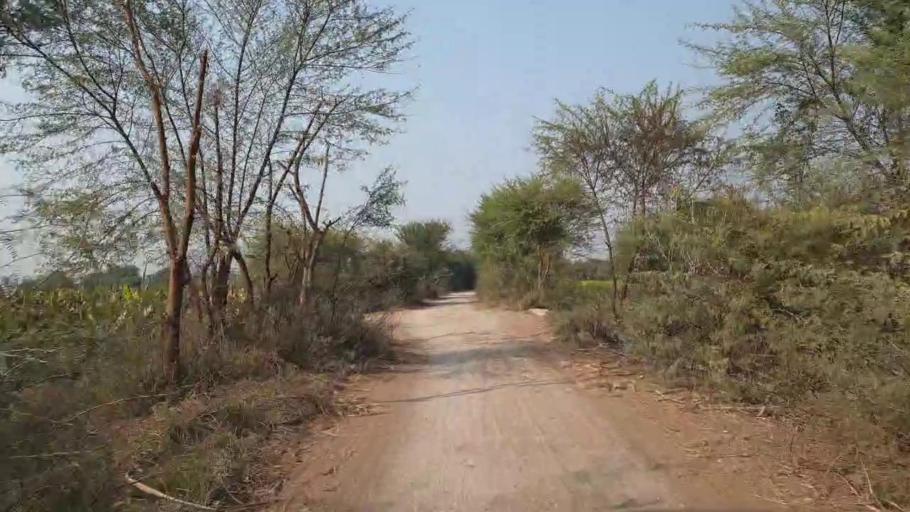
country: PK
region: Sindh
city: Bhit Shah
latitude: 25.8896
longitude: 68.4752
